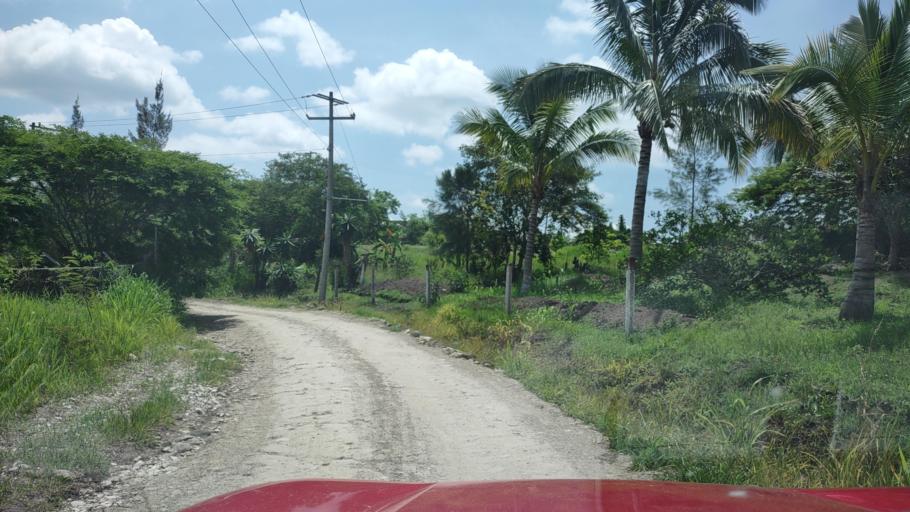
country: MX
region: Veracruz
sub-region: Emiliano Zapata
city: Dos Rios
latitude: 19.4626
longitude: -96.7900
